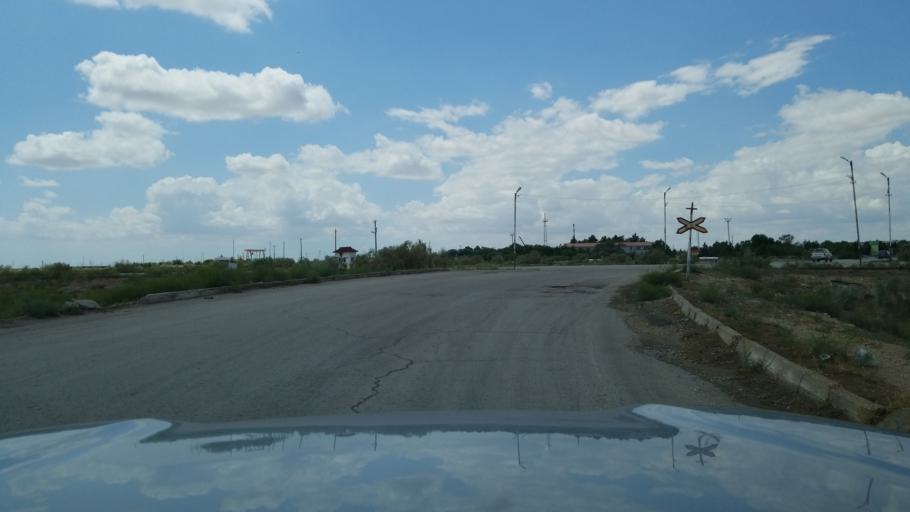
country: TM
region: Balkan
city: Balkanabat
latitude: 39.4967
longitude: 54.3488
